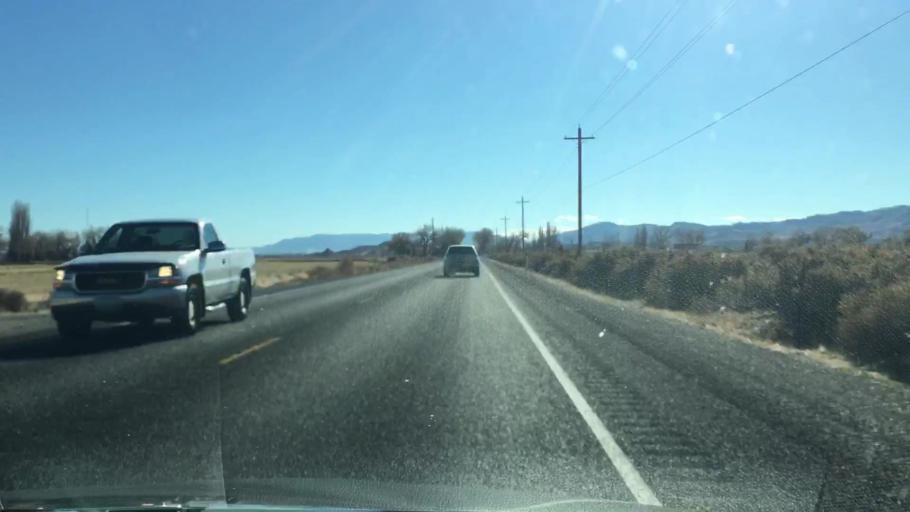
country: US
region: Nevada
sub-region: Lyon County
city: Yerington
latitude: 39.0560
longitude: -119.1814
